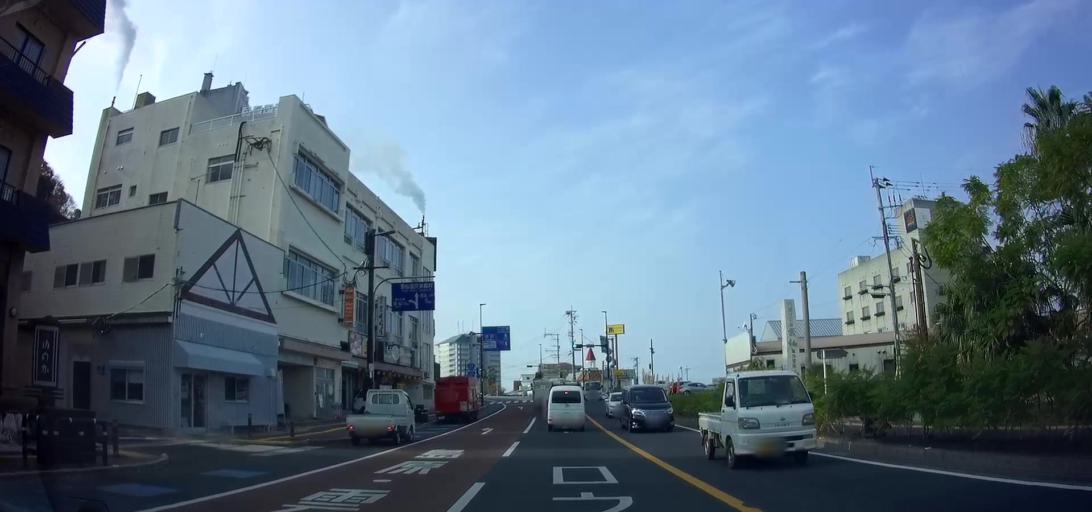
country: JP
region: Nagasaki
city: Shimabara
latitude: 32.7260
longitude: 130.2057
